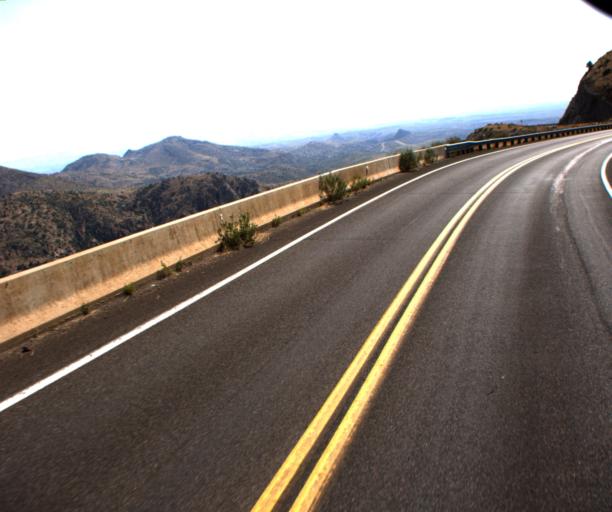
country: US
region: Arizona
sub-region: Greenlee County
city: Clifton
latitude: 33.0499
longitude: -109.0929
